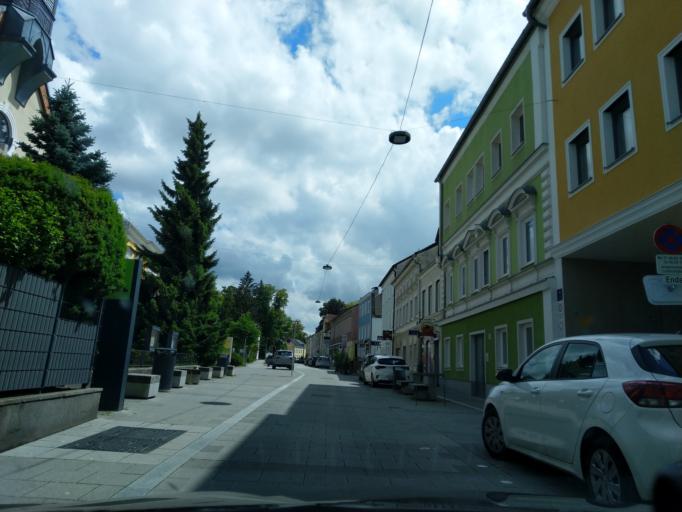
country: AT
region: Upper Austria
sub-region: Politischer Bezirk Ried im Innkreis
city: Ried im Innkreis
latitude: 48.2070
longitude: 13.4878
